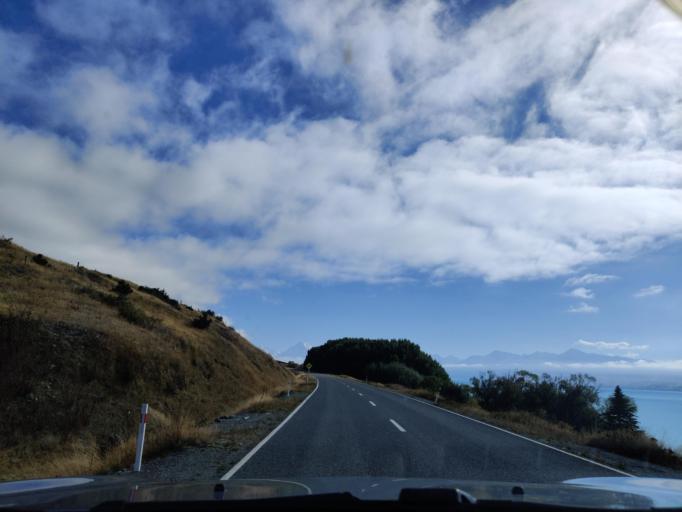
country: NZ
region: Canterbury
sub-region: Timaru District
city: Pleasant Point
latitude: -44.0487
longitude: 170.1341
